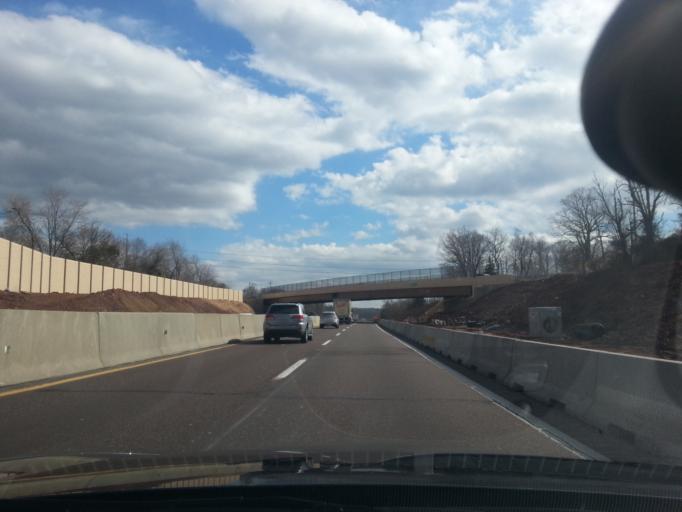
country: US
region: Pennsylvania
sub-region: Montgomery County
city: Kulpsville
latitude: 40.2115
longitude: -75.3247
